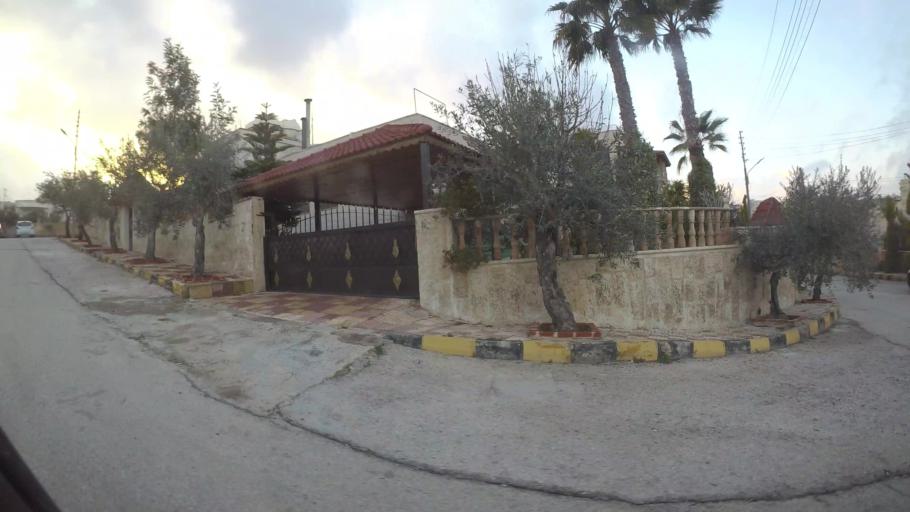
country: JO
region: Amman
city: Al Jubayhah
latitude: 32.0511
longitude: 35.9007
